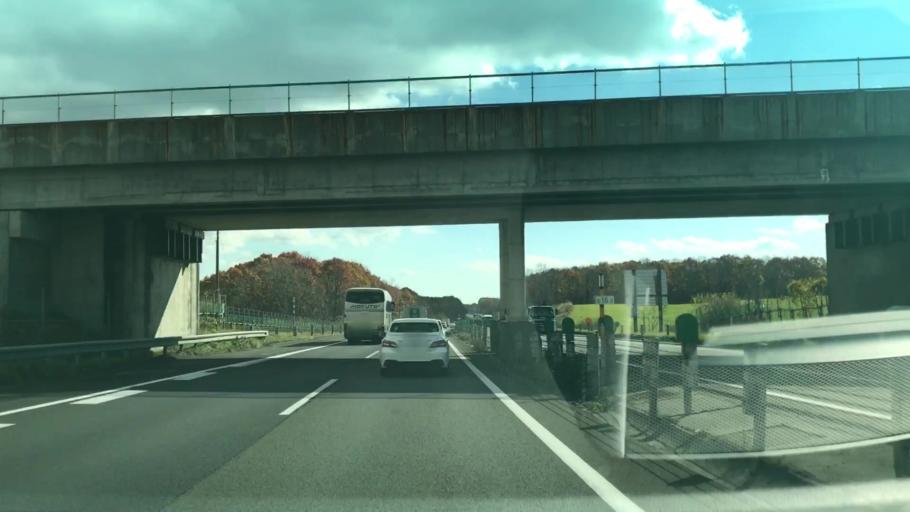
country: JP
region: Hokkaido
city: Kitahiroshima
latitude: 42.9481
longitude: 141.5156
